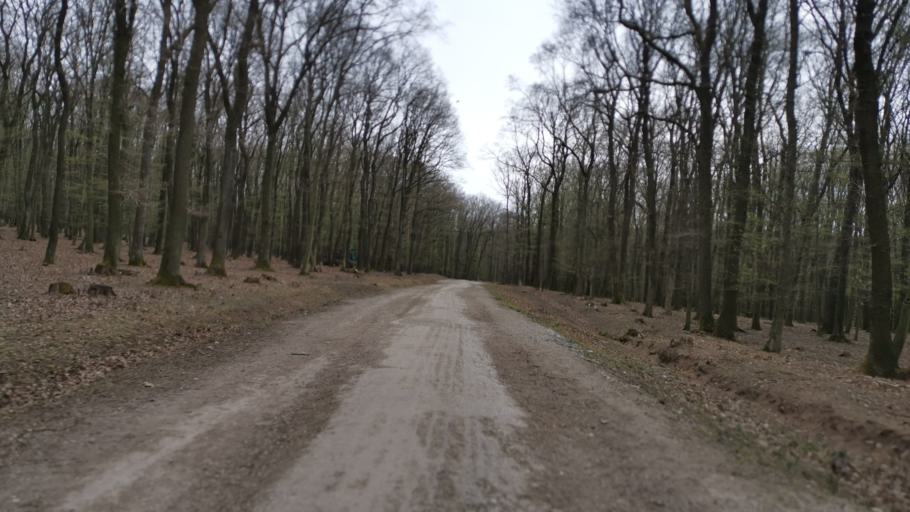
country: CZ
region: South Moravian
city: Petrov
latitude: 48.8272
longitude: 17.3057
